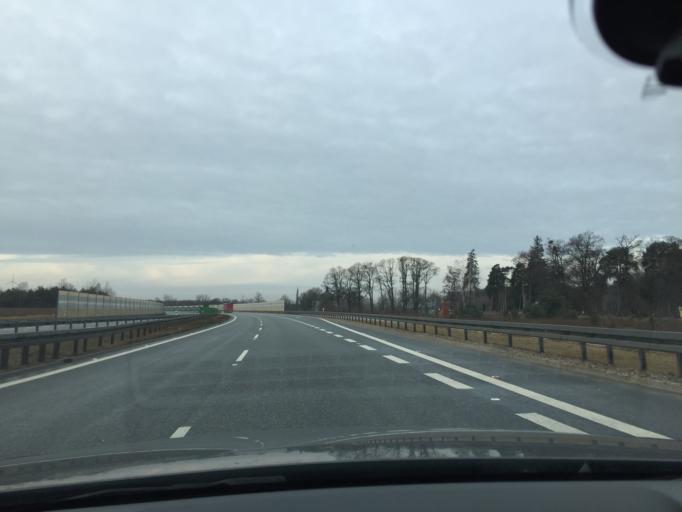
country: PL
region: Masovian Voivodeship
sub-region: Powiat zyrardowski
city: Radziejowice
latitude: 52.0040
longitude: 20.5690
